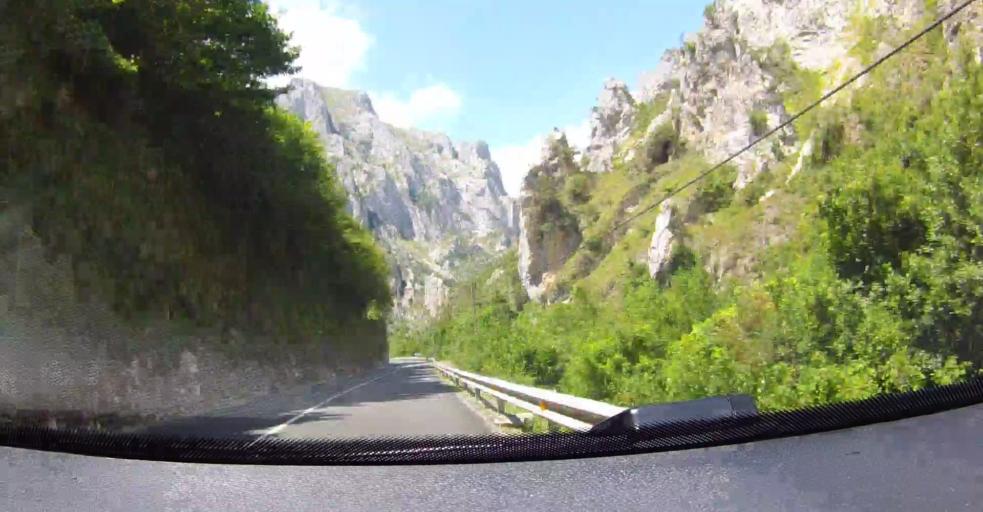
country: ES
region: Cantabria
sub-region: Provincia de Cantabria
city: Tresviso
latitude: 43.2647
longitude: -4.6247
